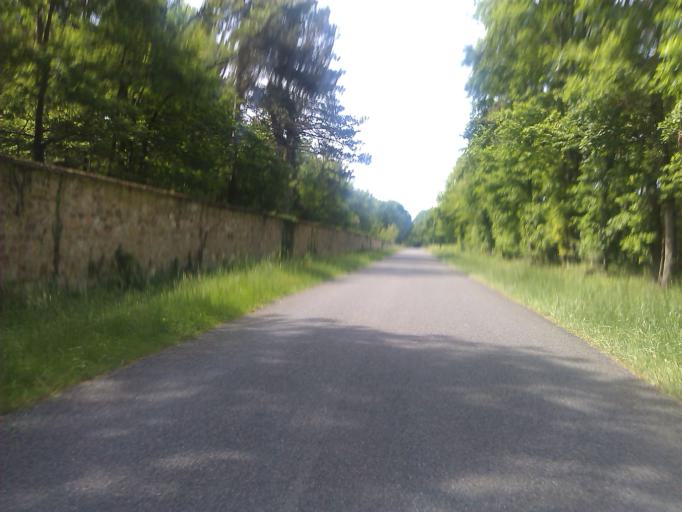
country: FR
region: Centre
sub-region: Departement du Cher
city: Orval
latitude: 46.5914
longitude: 2.4611
